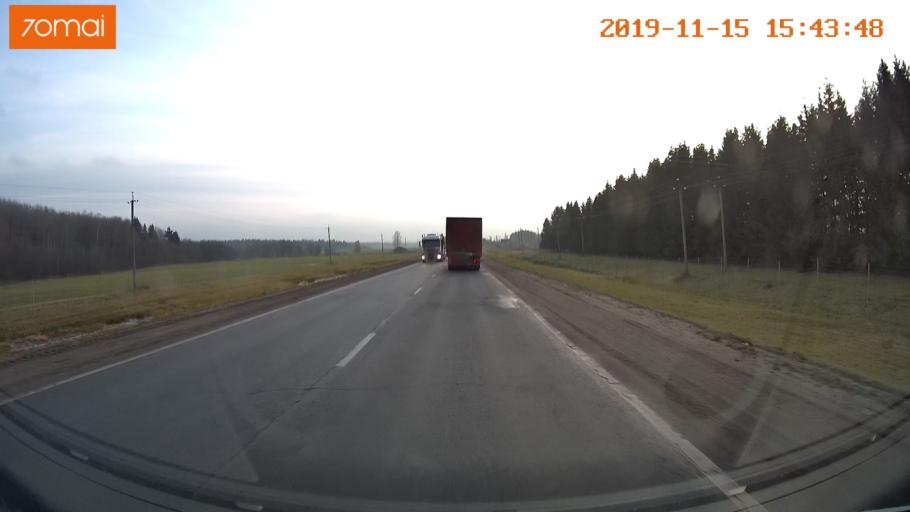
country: RU
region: Jaroslavl
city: Danilov
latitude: 57.9779
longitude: 40.0257
